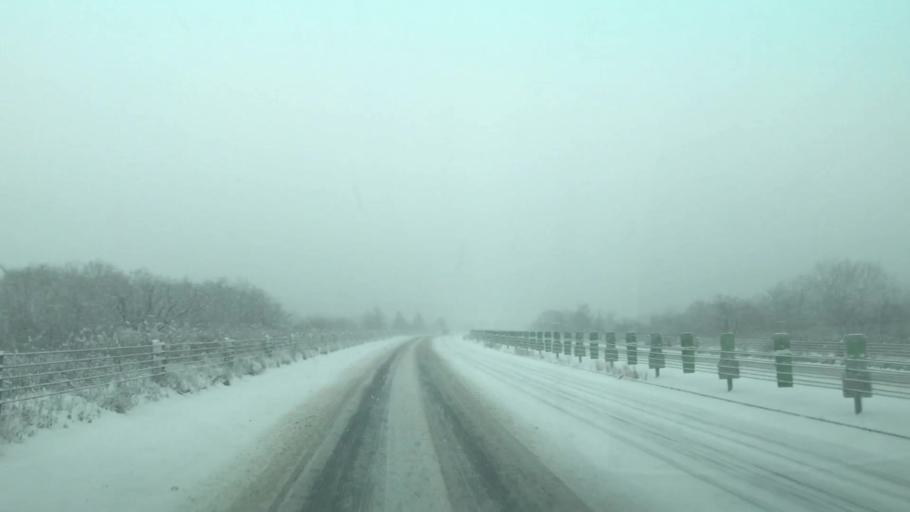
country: JP
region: Hokkaido
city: Shiraoi
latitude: 42.5072
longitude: 141.2691
